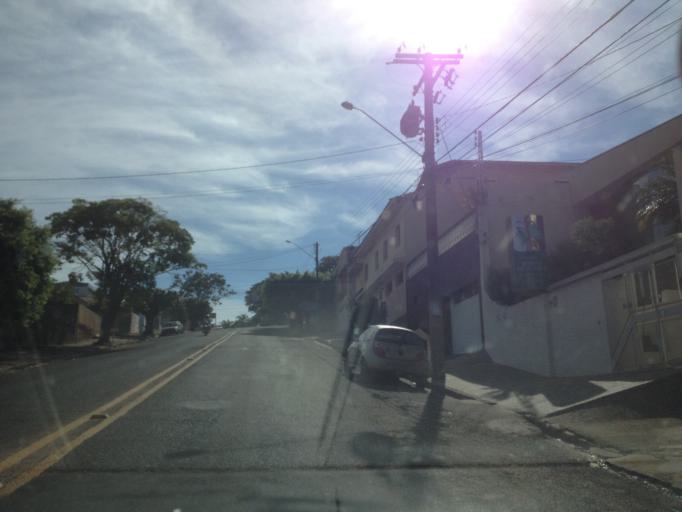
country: BR
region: Sao Paulo
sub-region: Marilia
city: Marilia
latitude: -22.2236
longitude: -49.9436
